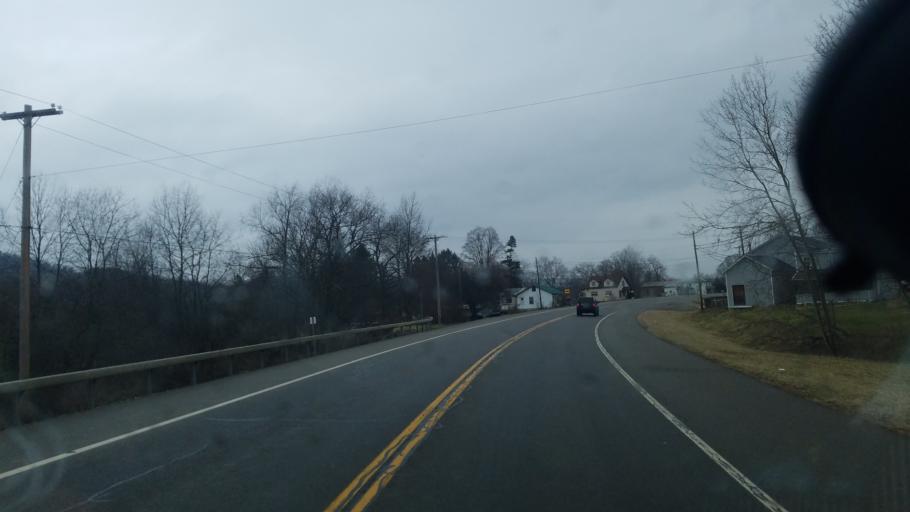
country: US
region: New York
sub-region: Allegany County
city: Wellsville
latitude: 42.0158
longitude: -77.8956
